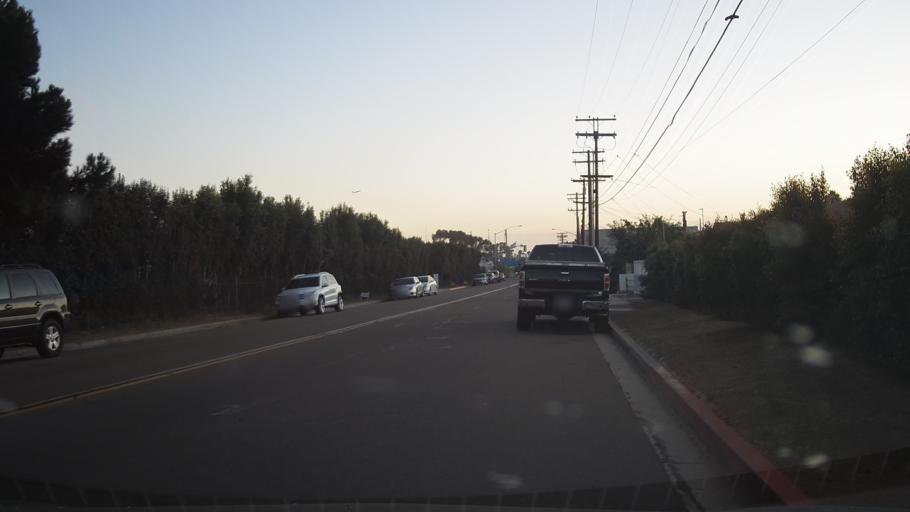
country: US
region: California
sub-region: San Diego County
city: San Diego
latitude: 32.7745
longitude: -117.2028
